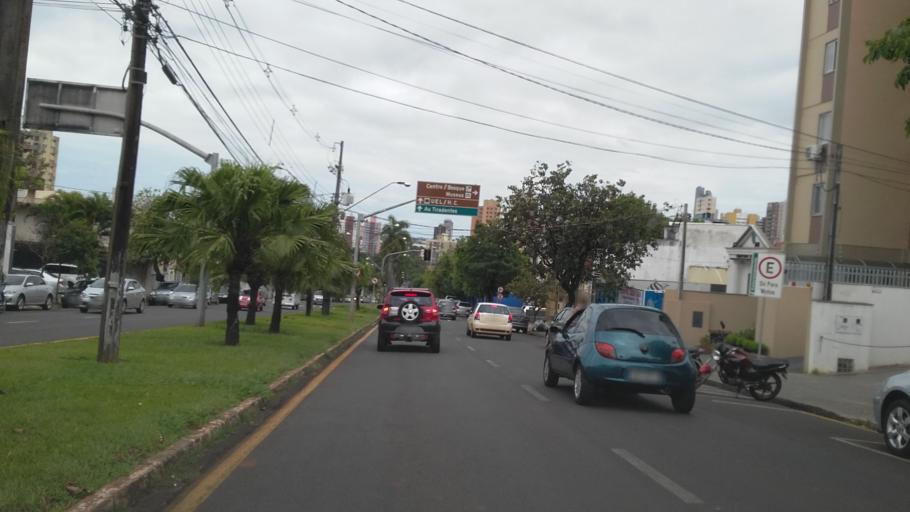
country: BR
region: Parana
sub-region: Londrina
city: Londrina
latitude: -23.3198
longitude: -51.1579
